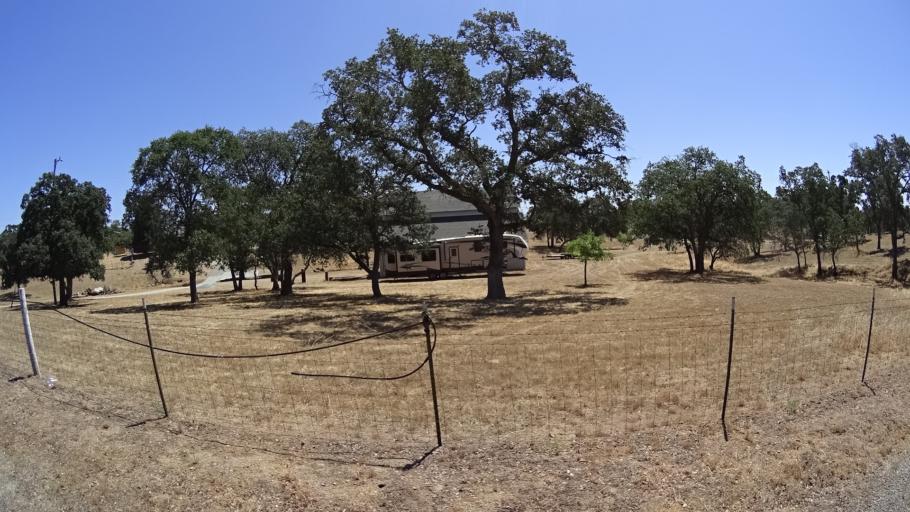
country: US
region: California
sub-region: Calaveras County
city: Rancho Calaveras
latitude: 38.1388
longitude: -120.9448
